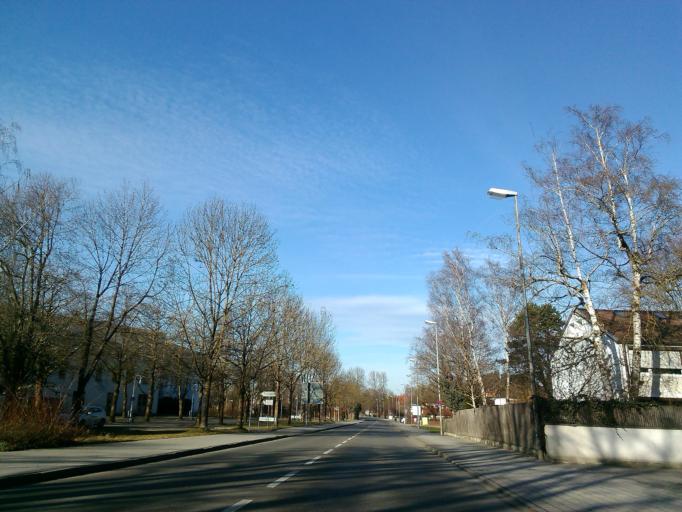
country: DE
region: Bavaria
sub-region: Upper Bavaria
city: Fuerstenfeldbruck
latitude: 48.1742
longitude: 11.2645
